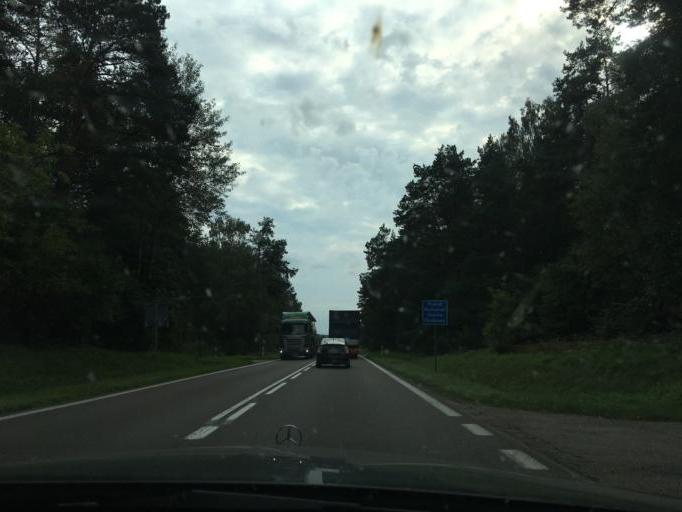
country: PL
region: Podlasie
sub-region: Powiat grajewski
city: Szczuczyn
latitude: 53.5209
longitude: 22.2514
